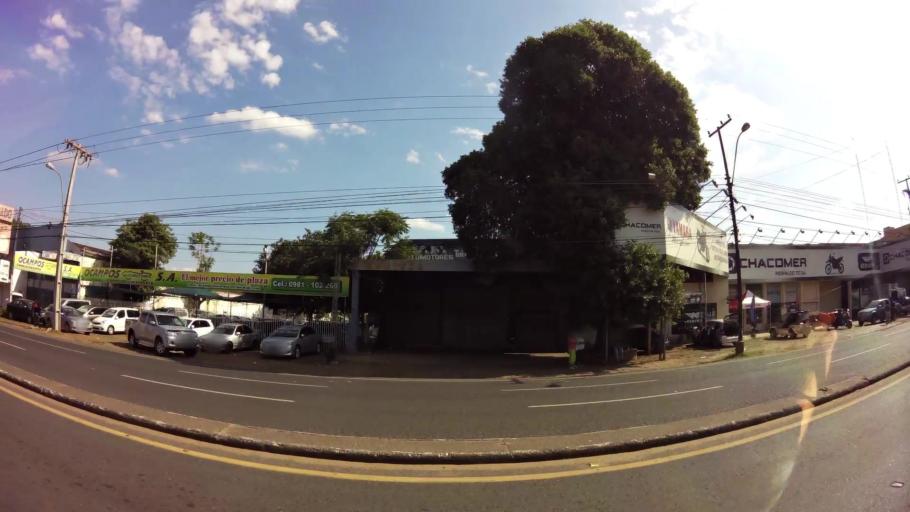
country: PY
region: Central
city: Fernando de la Mora
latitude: -25.3373
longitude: -57.5275
